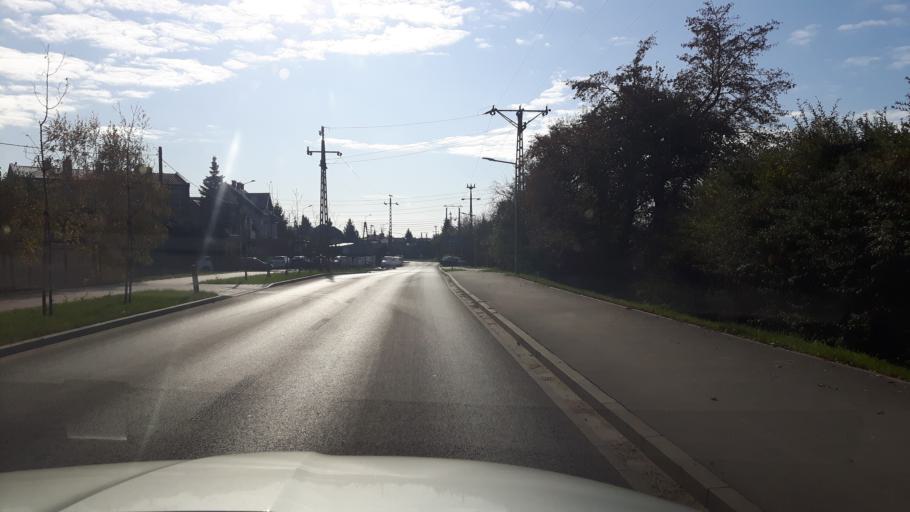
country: PL
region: Masovian Voivodeship
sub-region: Powiat wolominski
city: Zabki
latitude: 52.2935
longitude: 21.1000
